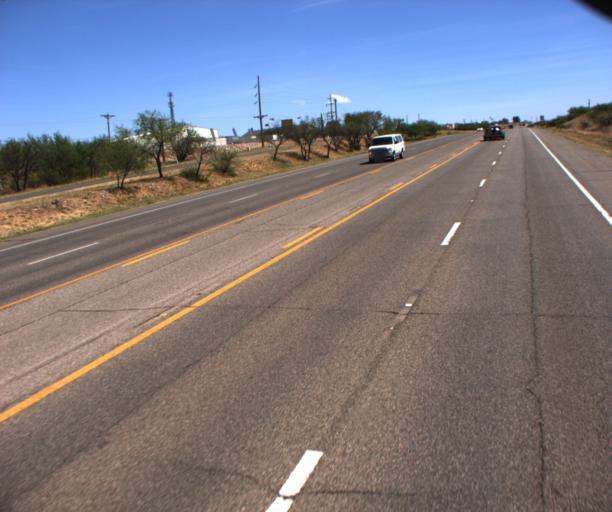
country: US
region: Arizona
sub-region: Cochise County
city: Huachuca City
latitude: 31.6390
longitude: -110.3382
